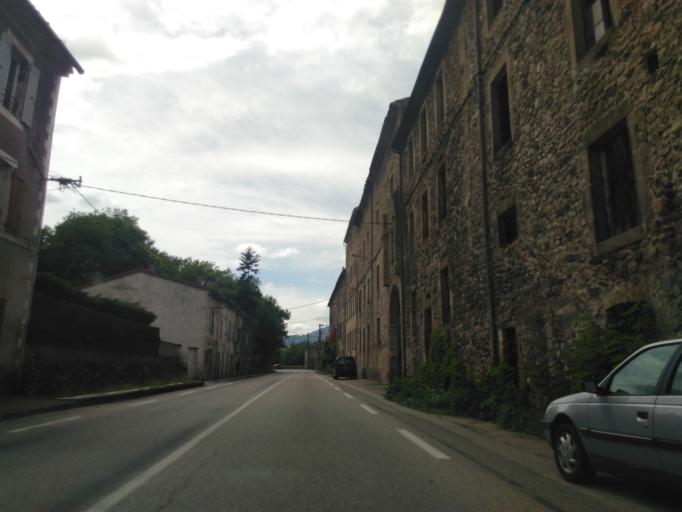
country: FR
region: Rhone-Alpes
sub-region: Departement de l'Ardeche
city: Labegude
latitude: 44.6449
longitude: 4.3506
